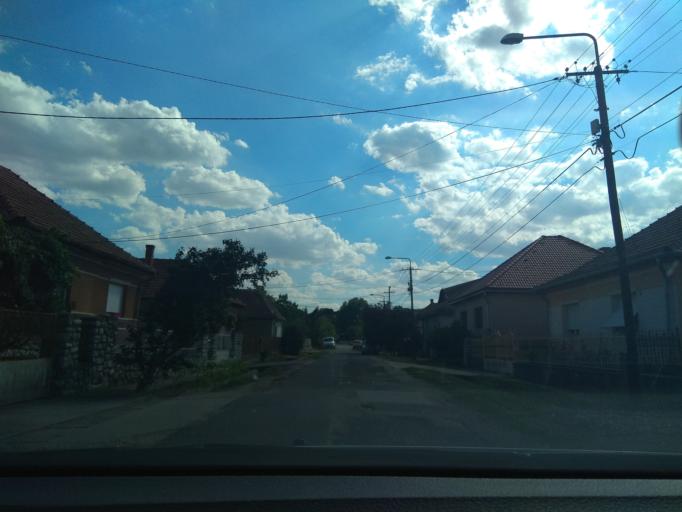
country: HU
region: Borsod-Abauj-Zemplen
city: Miskolc
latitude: 48.0573
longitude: 20.7919
